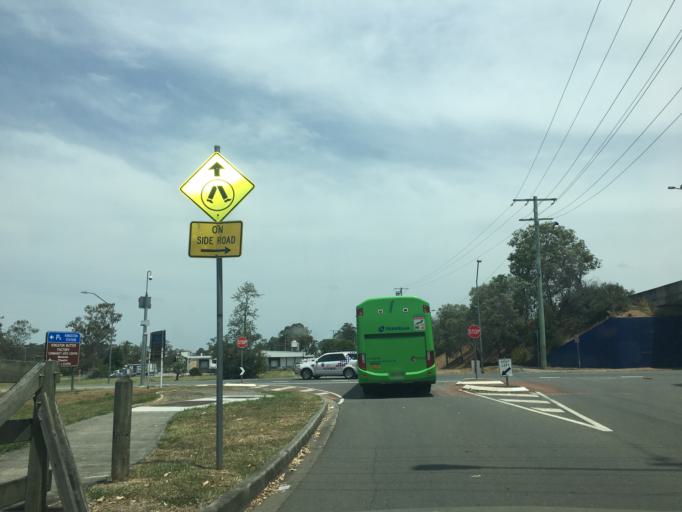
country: AU
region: Queensland
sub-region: Logan
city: Logan City
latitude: -27.6580
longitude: 153.1175
